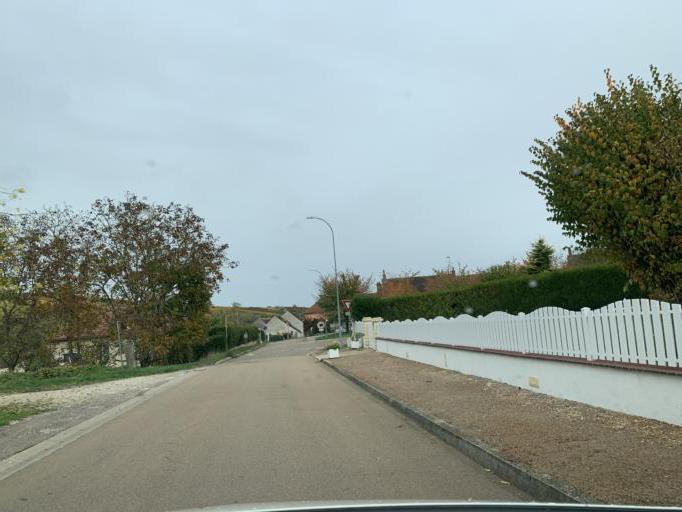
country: FR
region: Bourgogne
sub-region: Departement de l'Yonne
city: Champs-sur-Yonne
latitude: 47.7195
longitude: 3.5808
